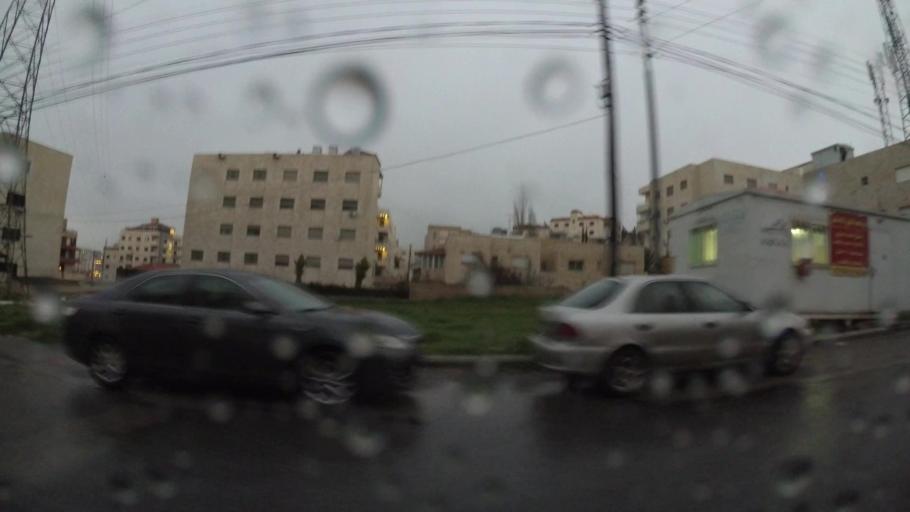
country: JO
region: Amman
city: Umm as Summaq
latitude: 31.9019
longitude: 35.8625
